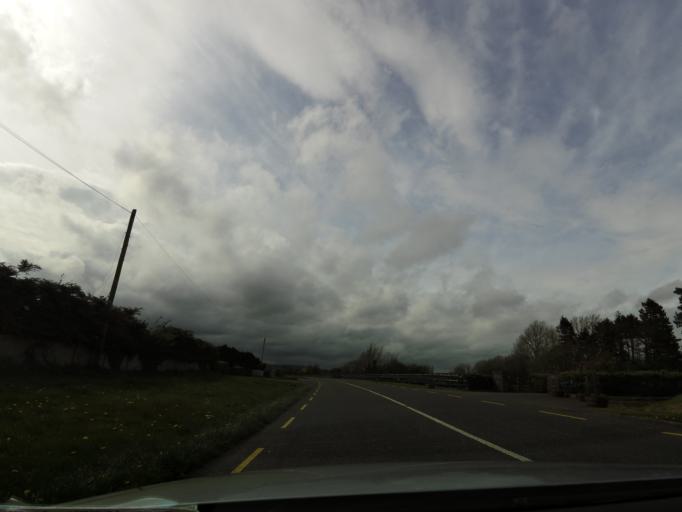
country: IE
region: Leinster
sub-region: Kilkenny
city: Ballyragget
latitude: 52.7286
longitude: -7.3790
